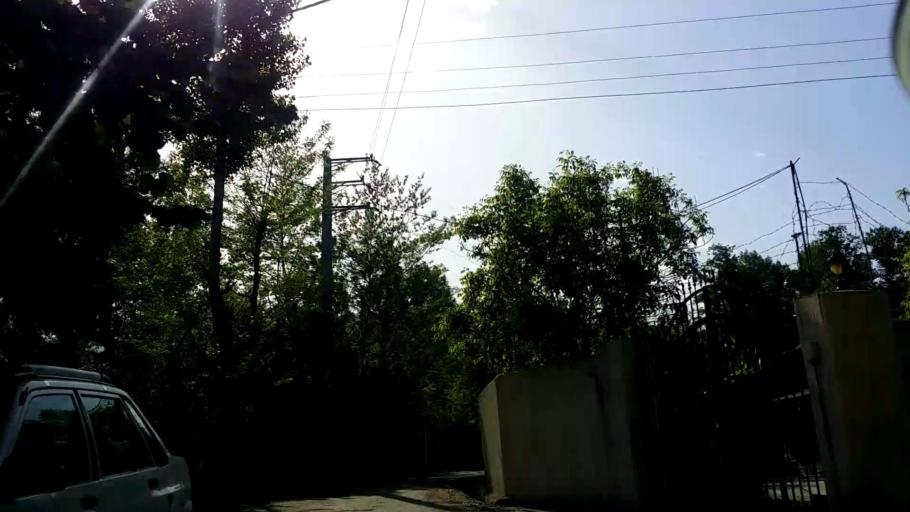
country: IR
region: Mazandaran
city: `Abbasabad
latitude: 36.5222
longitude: 51.1770
